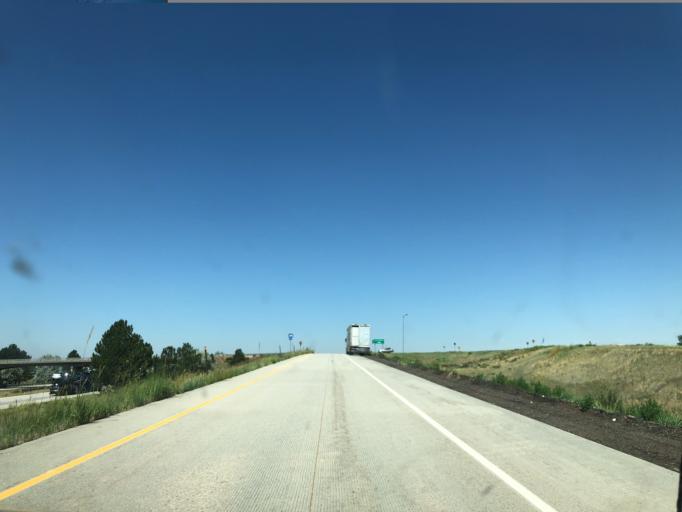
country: US
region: Colorado
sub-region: Adams County
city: Strasburg
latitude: 39.7345
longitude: -104.3238
